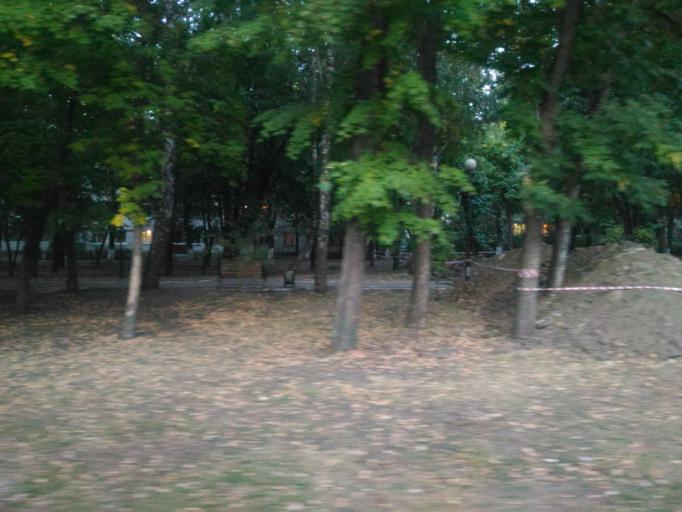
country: RU
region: Ulyanovsk
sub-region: Ulyanovskiy Rayon
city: Ulyanovsk
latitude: 54.3053
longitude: 48.3233
